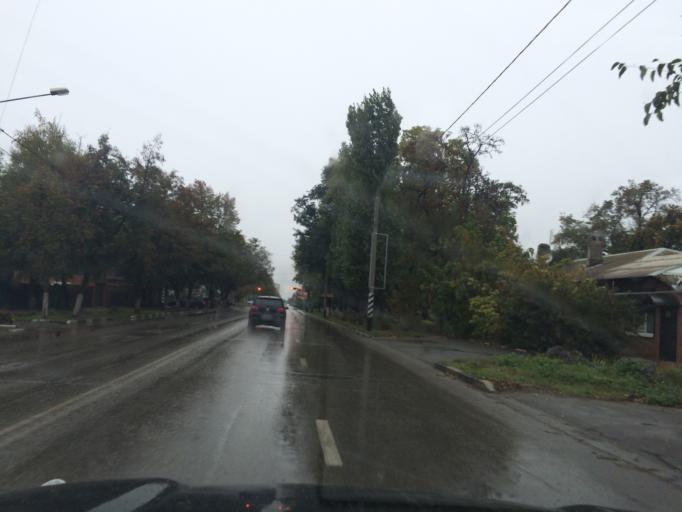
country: RU
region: Rostov
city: Azov
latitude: 47.0982
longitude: 39.4429
